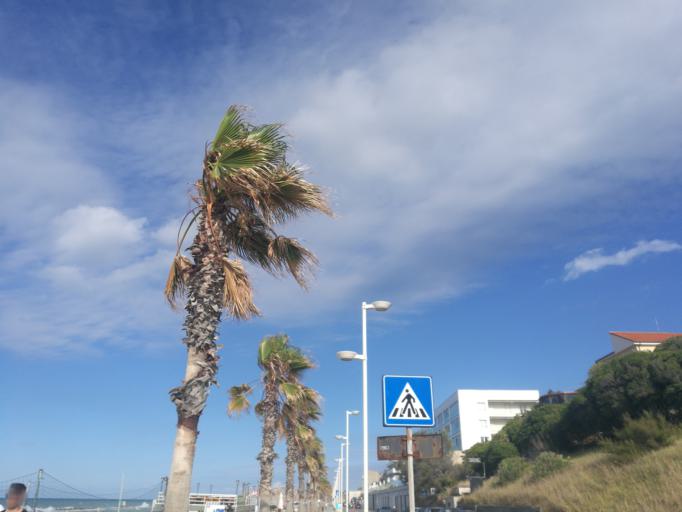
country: IT
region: Molise
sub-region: Provincia di Campobasso
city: Termoli
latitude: 42.0063
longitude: 14.9800
